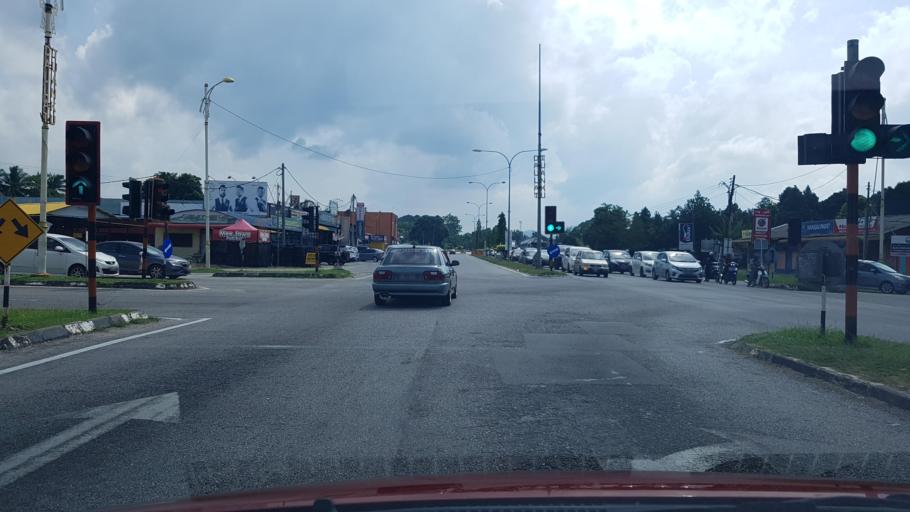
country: MY
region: Terengganu
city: Kuala Terengganu
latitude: 5.3395
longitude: 103.1020
